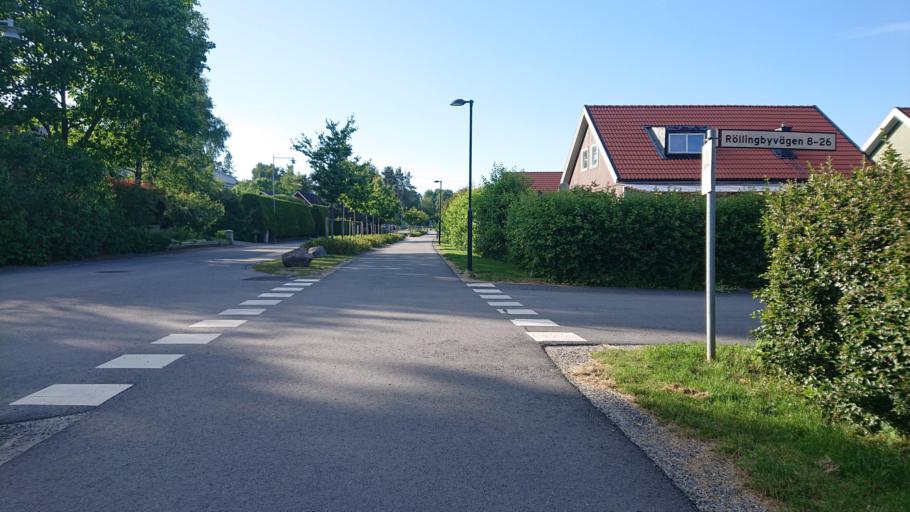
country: SE
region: Stockholm
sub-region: Osterakers Kommun
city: Akersberga
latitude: 59.4911
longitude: 18.2901
